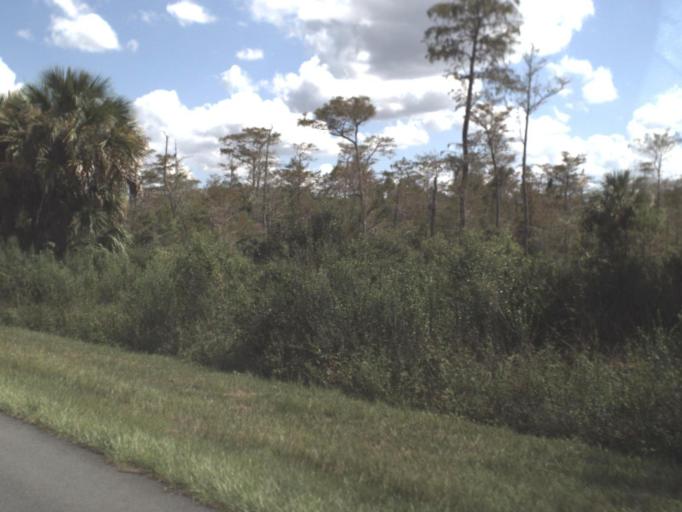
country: US
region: Florida
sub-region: Collier County
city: Marco
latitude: 25.8719
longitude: -81.1808
